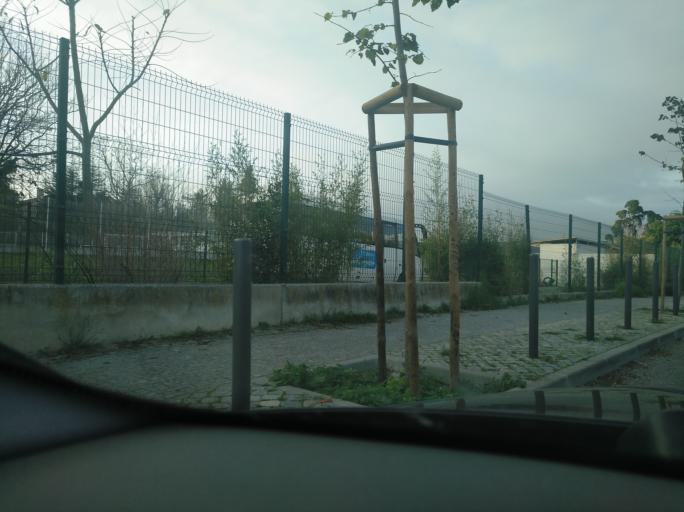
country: PT
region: Lisbon
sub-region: Odivelas
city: Olival do Basto
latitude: 38.7730
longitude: -9.1701
